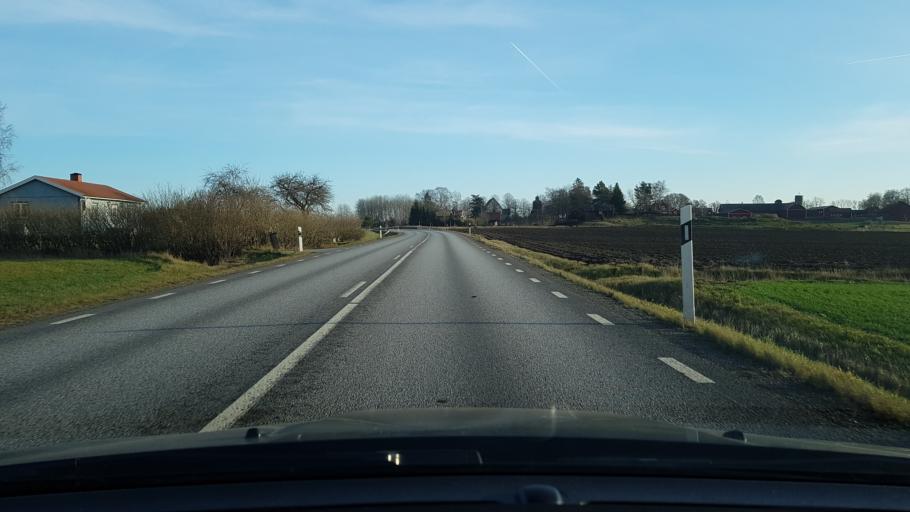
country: SE
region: Stockholm
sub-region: Sigtuna Kommun
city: Marsta
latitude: 59.7515
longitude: 18.0091
